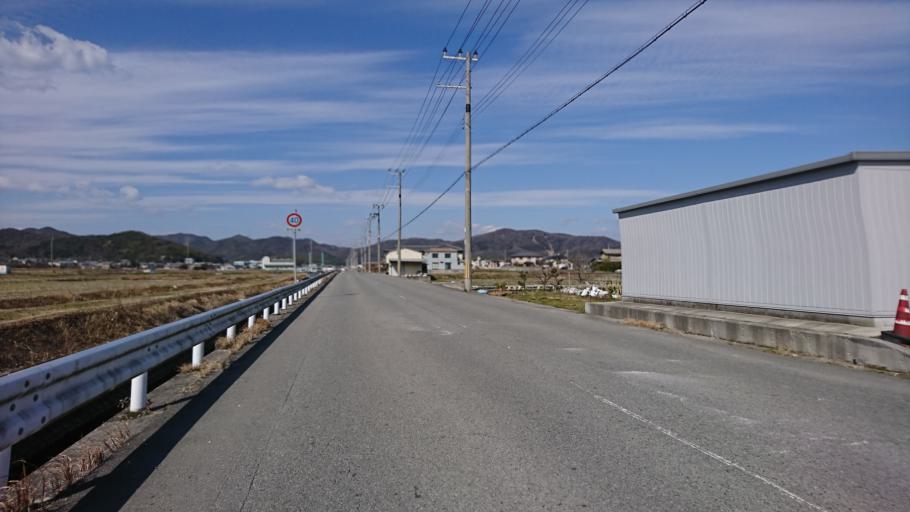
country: JP
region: Hyogo
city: Kakogawacho-honmachi
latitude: 34.8067
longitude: 134.8102
